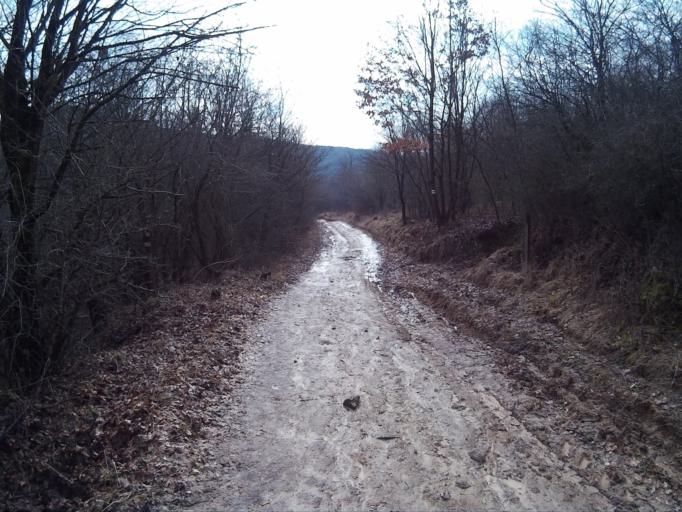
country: HU
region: Borsod-Abauj-Zemplen
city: Satoraljaujhely
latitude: 48.4056
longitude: 21.6006
